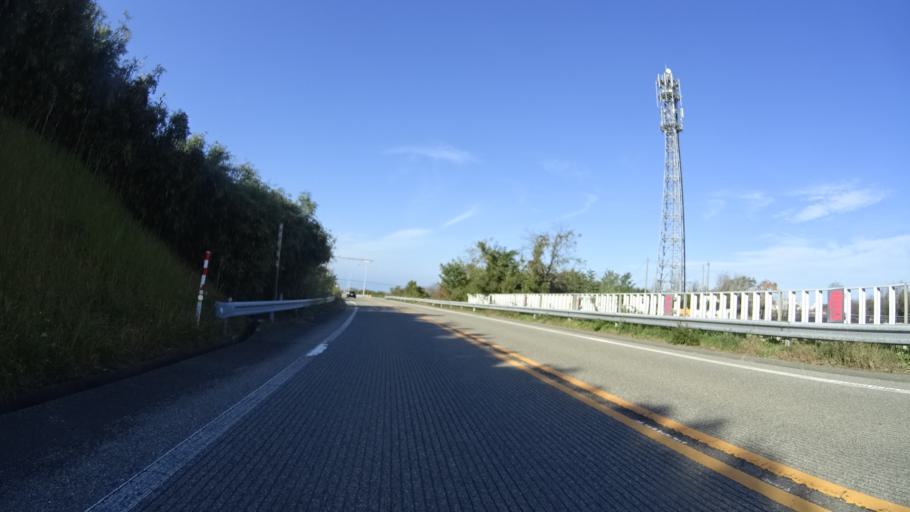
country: JP
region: Ishikawa
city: Kanazawa-shi
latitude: 36.6472
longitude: 136.6366
